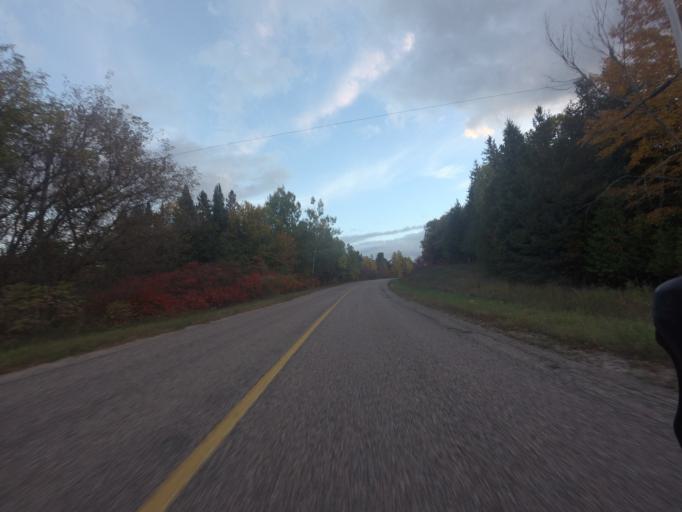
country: CA
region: Ontario
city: Renfrew
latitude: 45.4071
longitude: -76.9509
